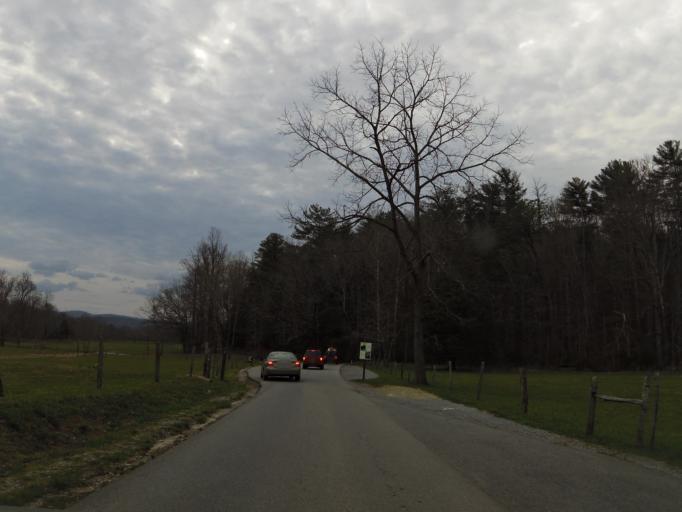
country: US
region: Tennessee
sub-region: Blount County
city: Wildwood
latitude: 35.6069
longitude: -83.7867
